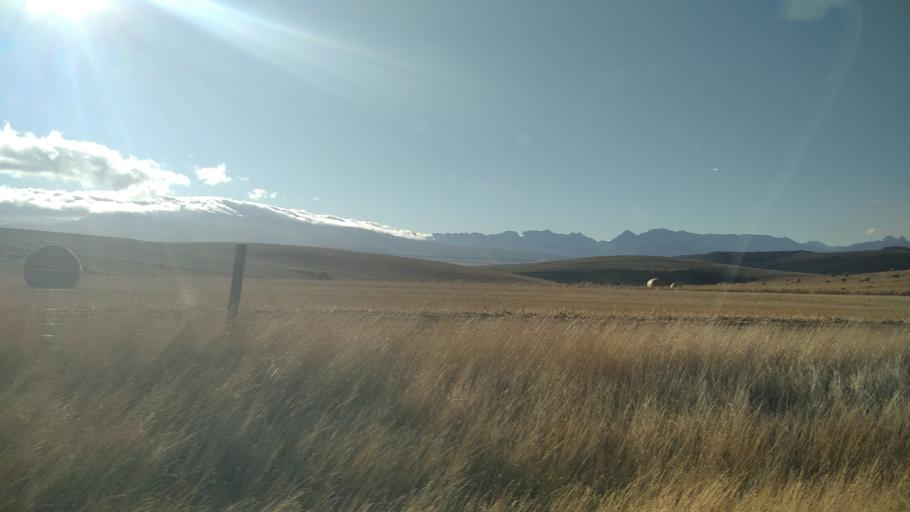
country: ZA
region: Western Cape
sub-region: Overberg District Municipality
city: Caledon
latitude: -34.1336
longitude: 19.2959
